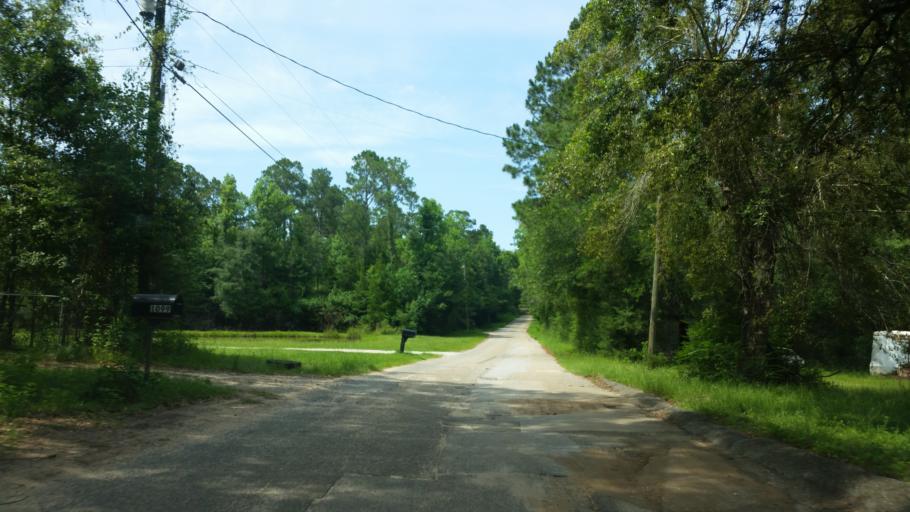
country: US
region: Florida
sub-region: Escambia County
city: Cantonment
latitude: 30.6278
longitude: -87.3829
